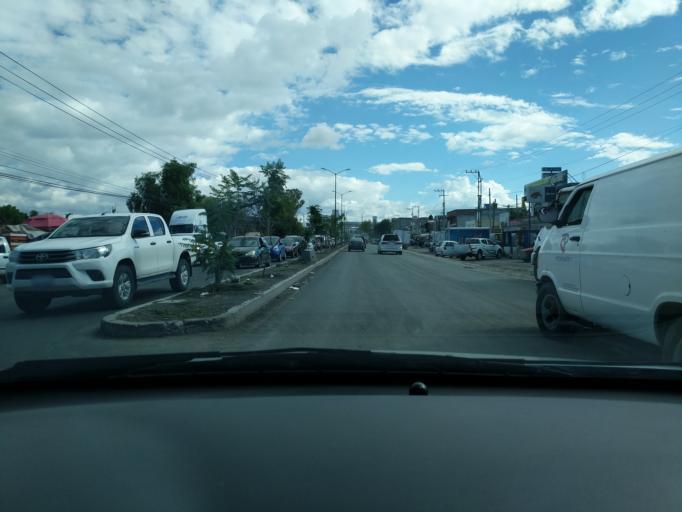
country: MX
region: Queretaro
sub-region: El Marques
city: General Lazaro Cardenas (El Colorado)
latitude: 20.5778
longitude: -100.2562
